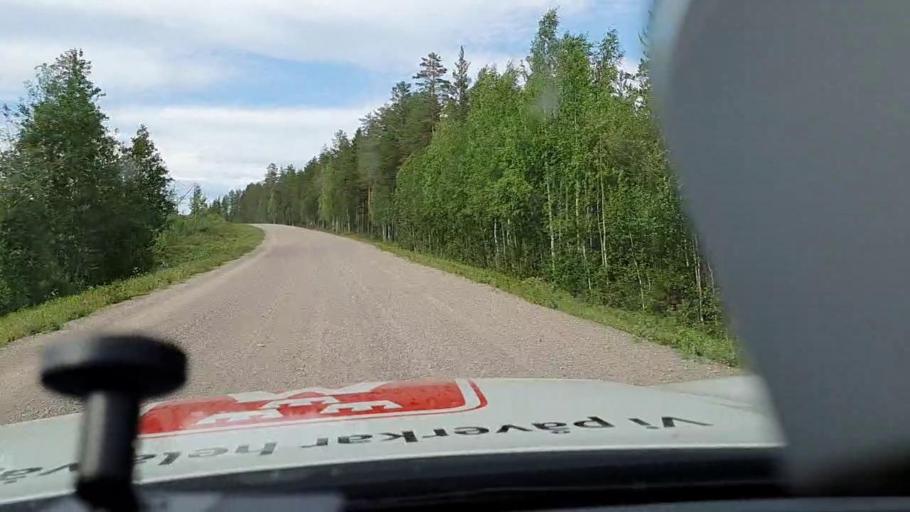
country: SE
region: Norrbotten
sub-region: Alvsbyns Kommun
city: AElvsbyn
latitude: 66.1295
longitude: 20.9984
